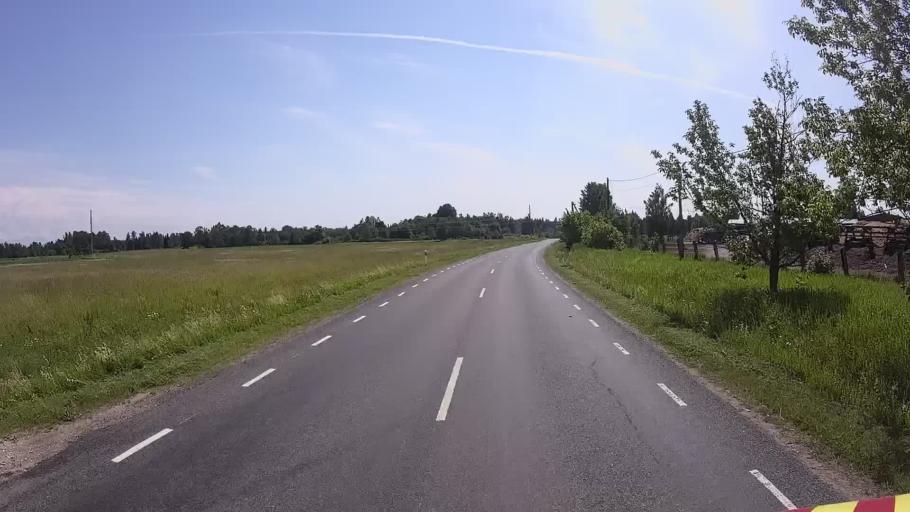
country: EE
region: Viljandimaa
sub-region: Karksi vald
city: Karksi-Nuia
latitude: 58.0950
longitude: 25.5608
